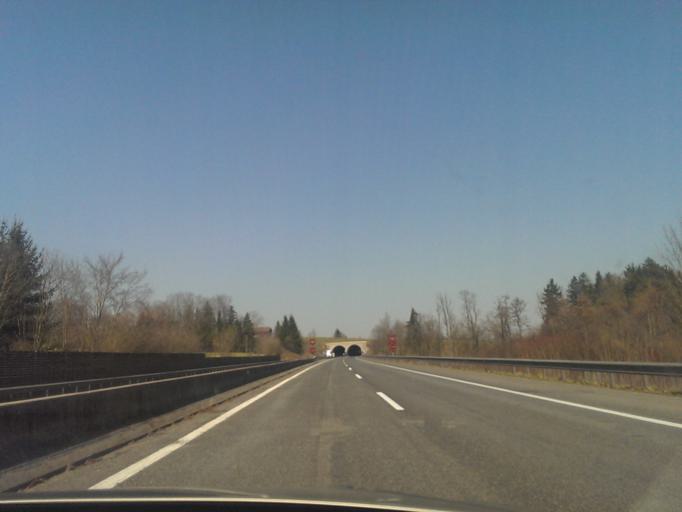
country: AT
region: Upper Austria
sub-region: Politischer Bezirk Kirchdorf an der Krems
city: Kremsmunster
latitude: 47.9692
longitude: 14.0946
